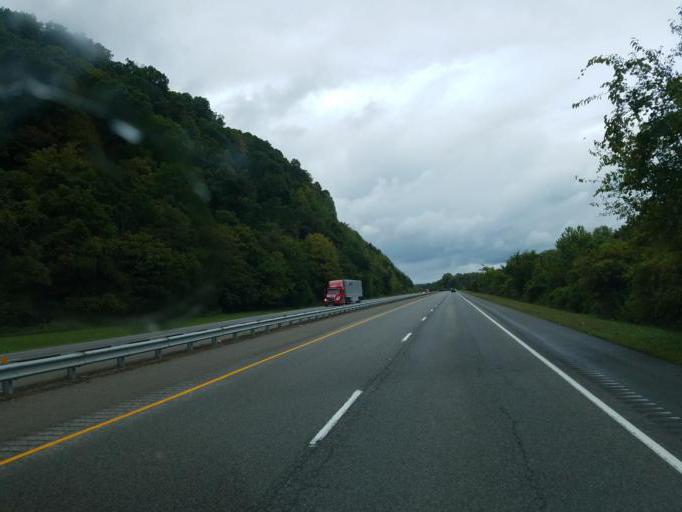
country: US
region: Ohio
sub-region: Scioto County
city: Wheelersburg
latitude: 38.7087
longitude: -82.8798
